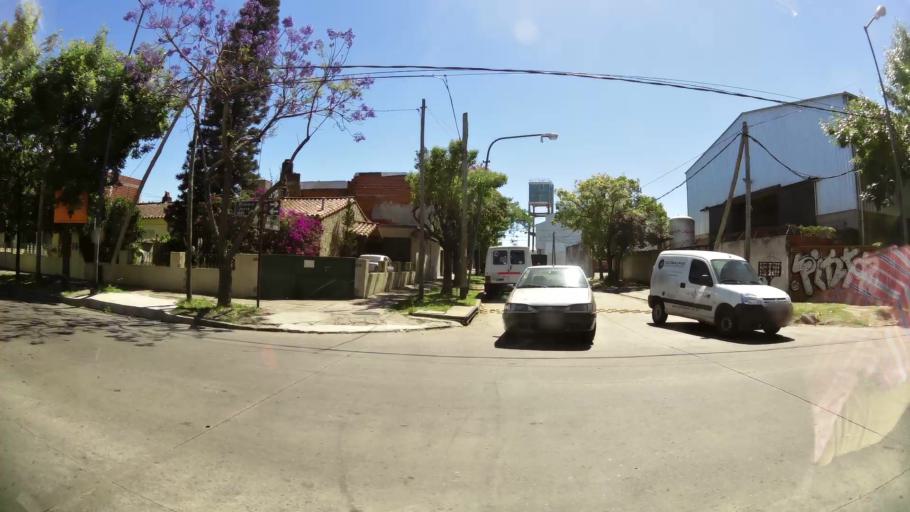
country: AR
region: Buenos Aires
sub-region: Partido de General San Martin
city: General San Martin
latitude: -34.5408
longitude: -58.5416
